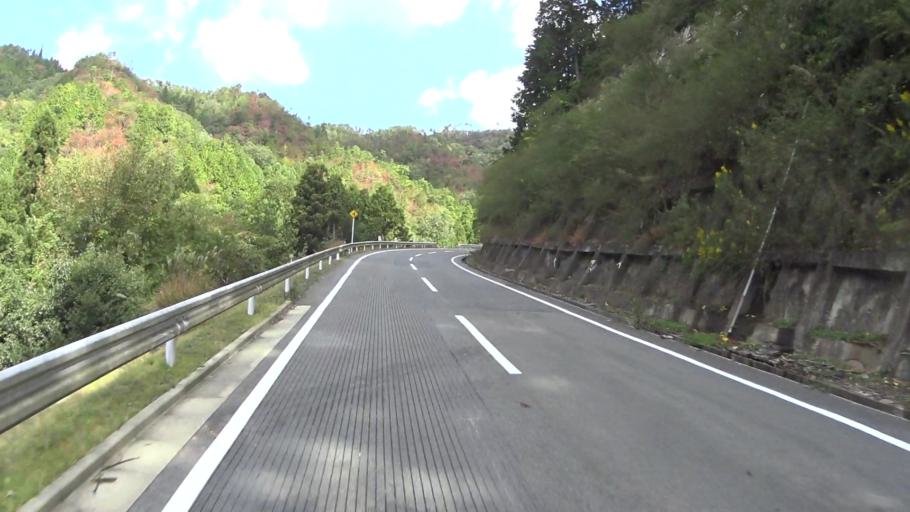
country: JP
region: Kyoto
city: Kameoka
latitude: 35.1037
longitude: 135.5539
